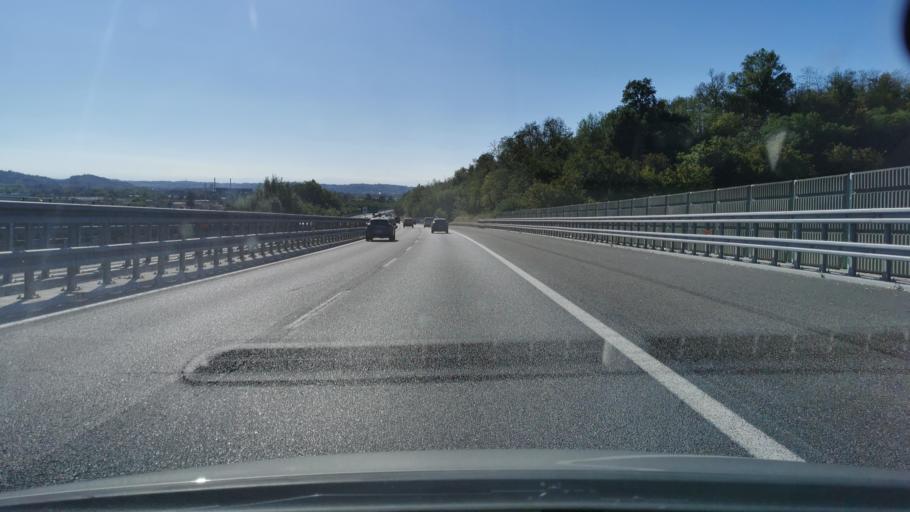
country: IT
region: Piedmont
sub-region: Provincia di Asti
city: Rocca d'Arazzo
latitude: 44.9110
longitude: 8.2890
